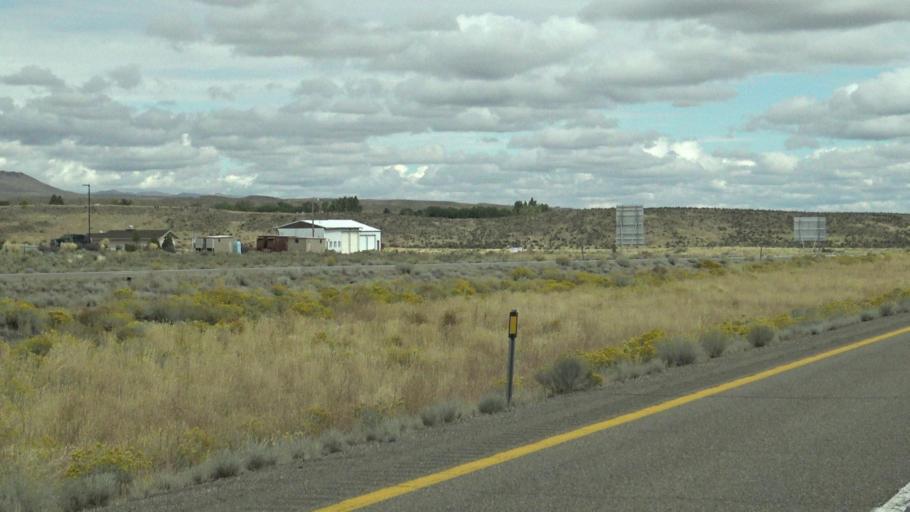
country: US
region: Nevada
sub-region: Elko County
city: Elko
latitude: 40.8666
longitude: -115.7316
